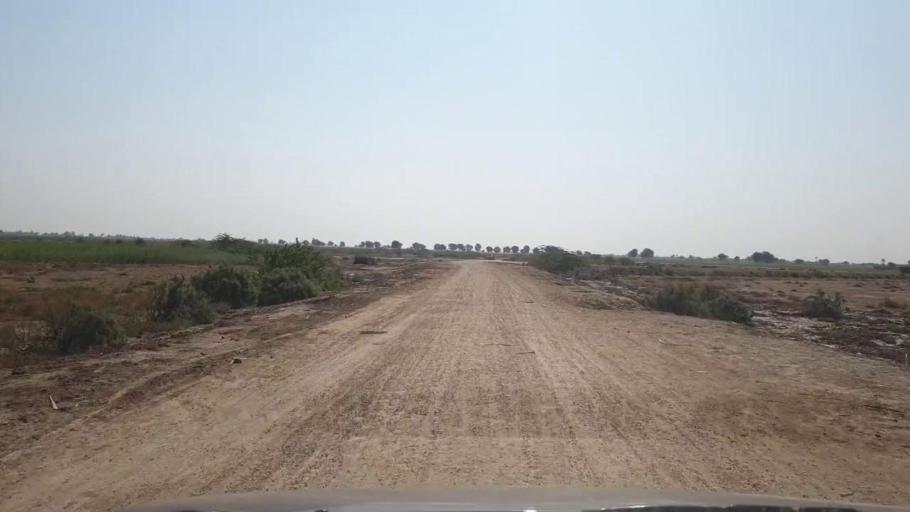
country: PK
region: Sindh
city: Samaro
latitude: 25.2414
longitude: 69.2878
